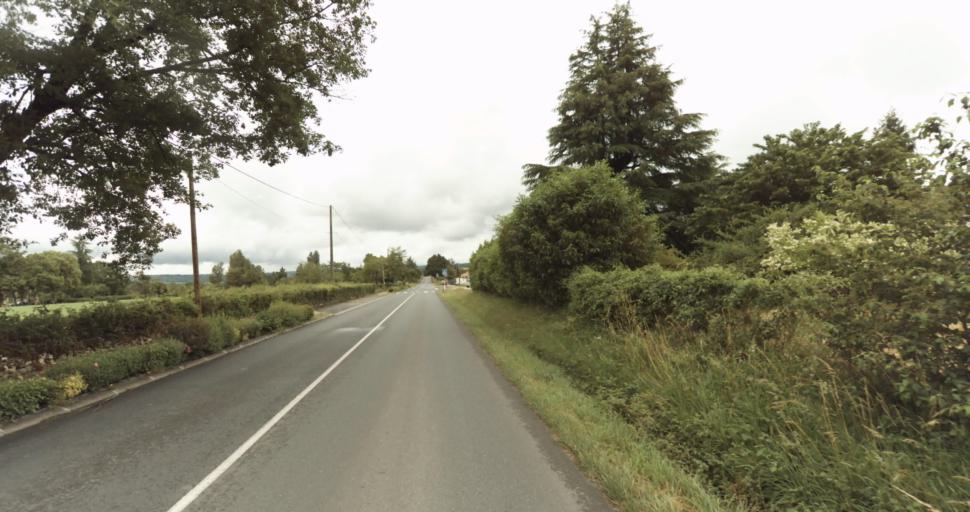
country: FR
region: Aquitaine
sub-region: Departement de la Dordogne
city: Beaumont-du-Perigord
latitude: 44.7579
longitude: 0.7720
